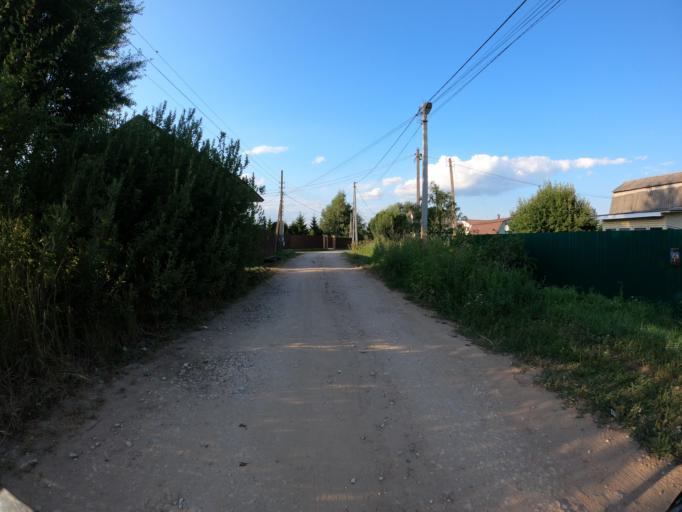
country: RU
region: Moskovskaya
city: Bronnitsy
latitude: 55.4833
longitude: 38.2588
